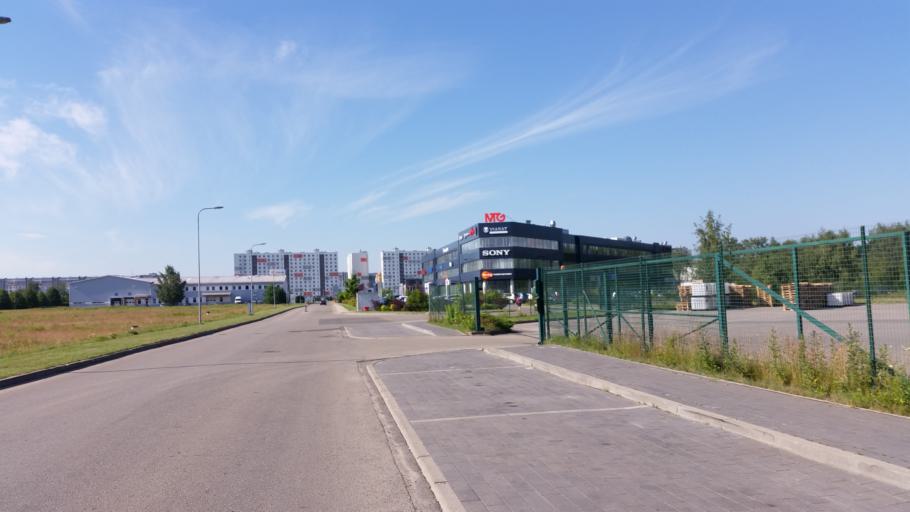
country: LV
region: Stopini
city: Ulbroka
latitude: 56.9518
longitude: 24.2183
